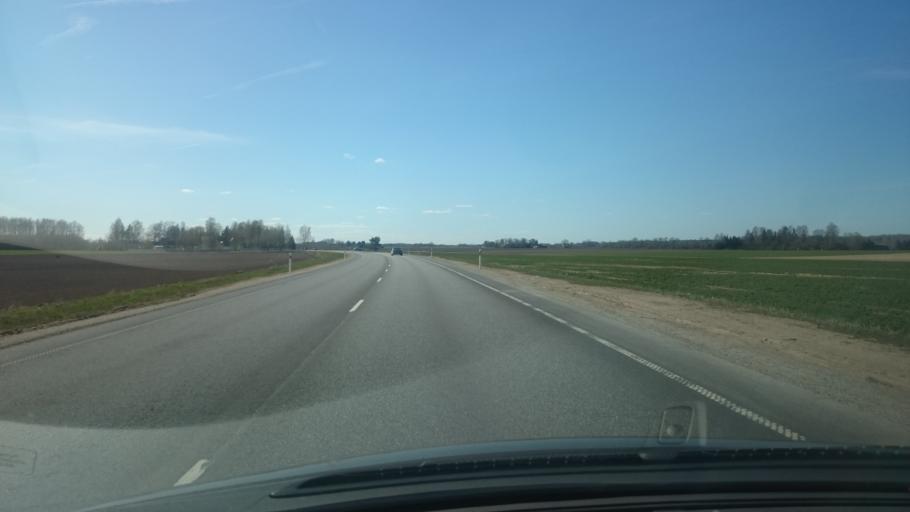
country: EE
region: Tartu
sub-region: Tartu linn
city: Tartu
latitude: 58.3716
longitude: 26.8734
